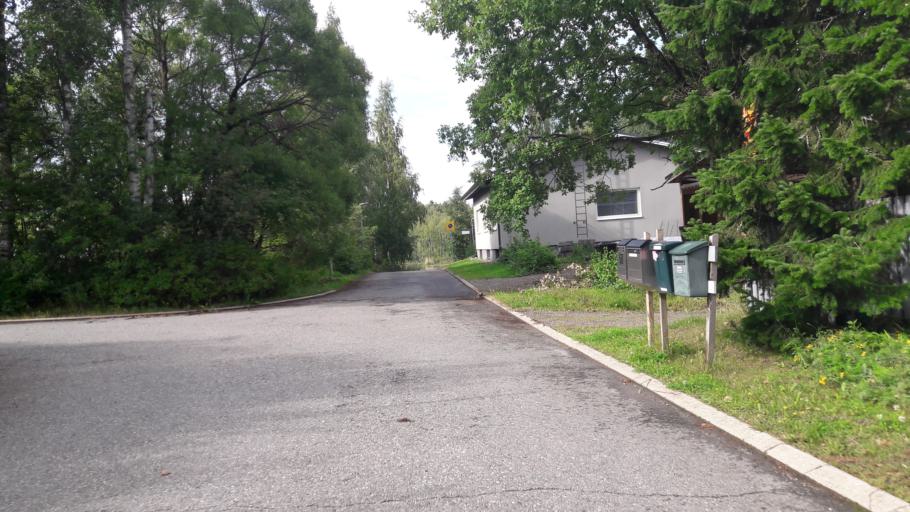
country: FI
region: North Karelia
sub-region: Joensuu
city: Joensuu
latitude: 62.5983
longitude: 29.7901
